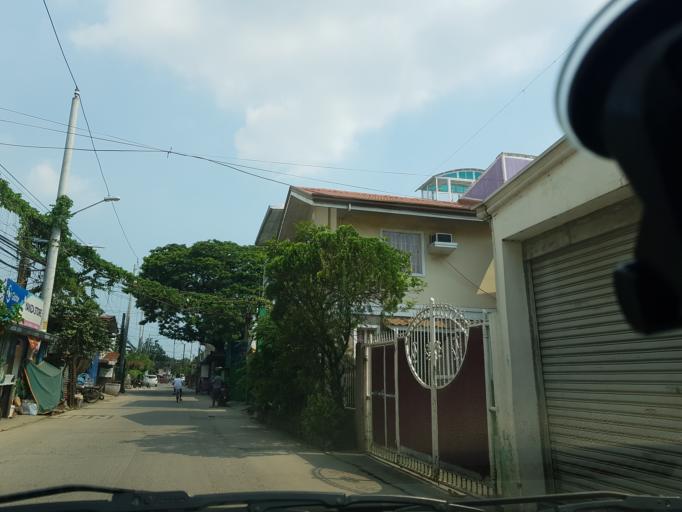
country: PH
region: Calabarzon
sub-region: Province of Rizal
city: Pateros
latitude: 14.5464
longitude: 121.0768
